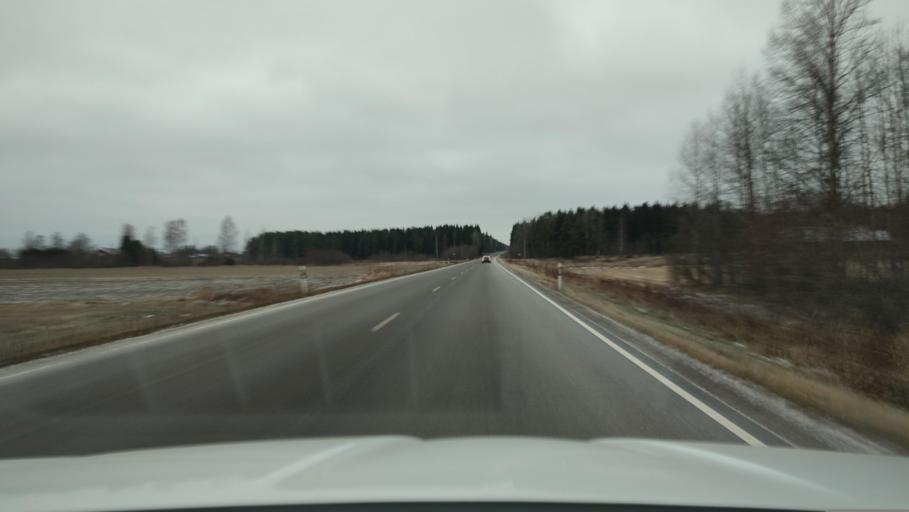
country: FI
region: Ostrobothnia
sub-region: Sydosterbotten
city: Naerpes
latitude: 62.5464
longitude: 21.4700
